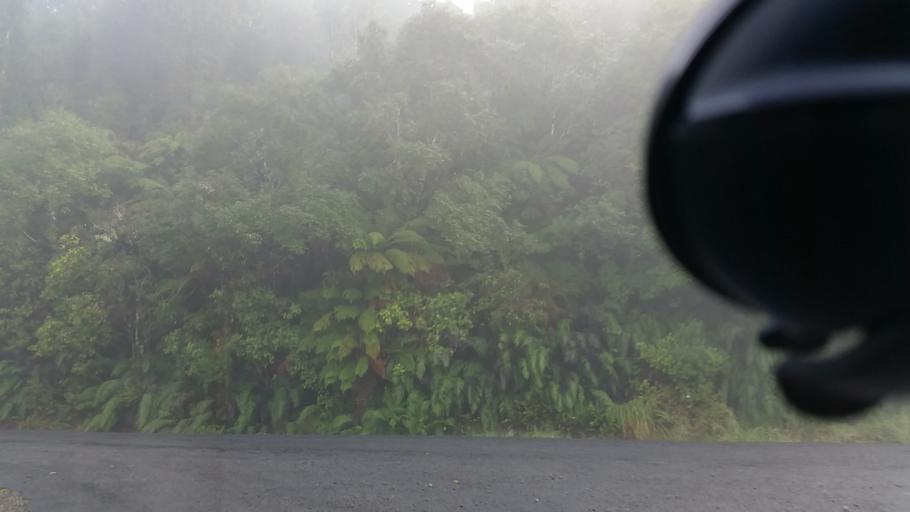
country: NZ
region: Taranaki
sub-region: New Plymouth District
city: Waitara
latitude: -38.9591
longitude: 174.7815
